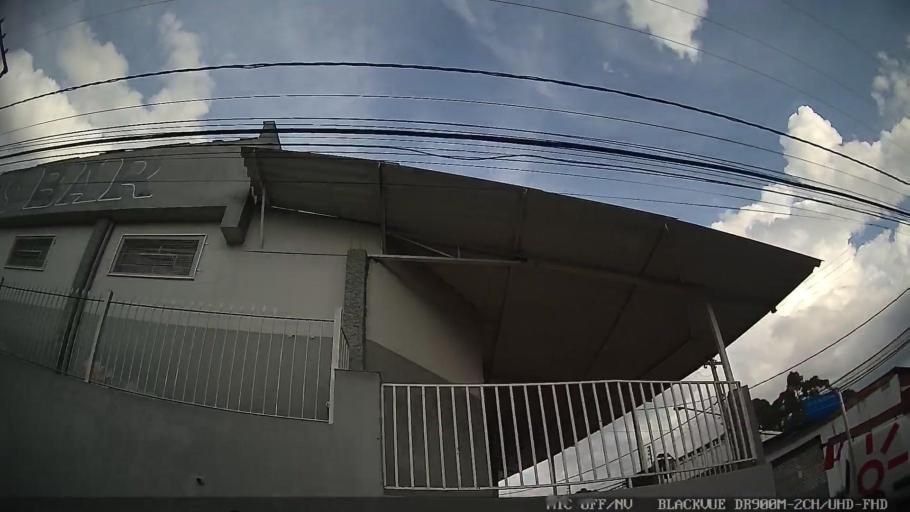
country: BR
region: Sao Paulo
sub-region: Braganca Paulista
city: Braganca Paulista
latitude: -22.9300
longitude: -46.5326
